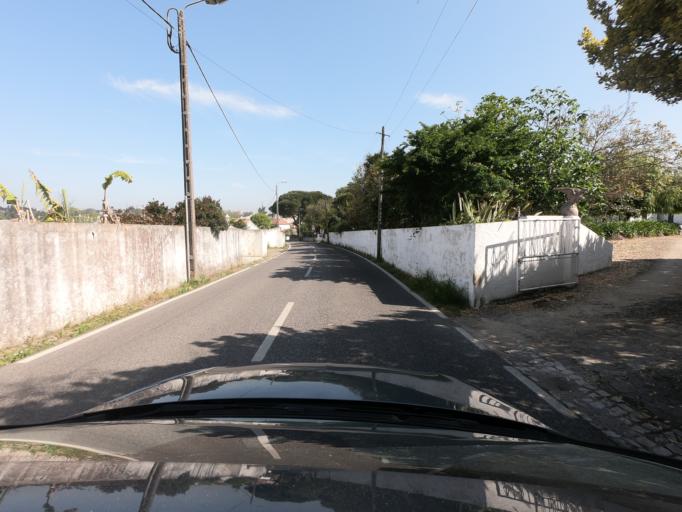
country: PT
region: Lisbon
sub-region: Sintra
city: Sintra
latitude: 38.8049
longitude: -9.3967
